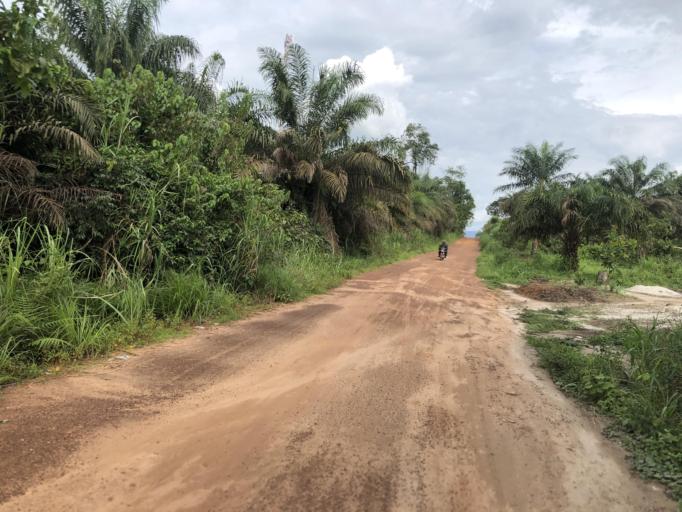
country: SL
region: Northern Province
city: Masaka
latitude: 8.7512
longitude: -11.8441
